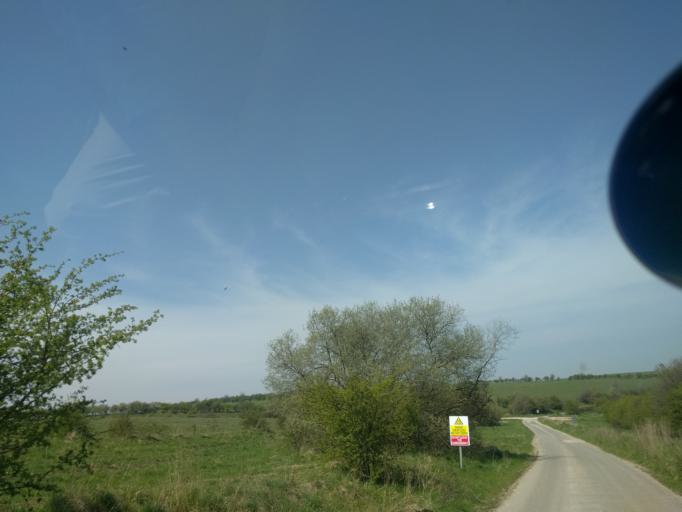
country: GB
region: England
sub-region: Wiltshire
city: Edington
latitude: 51.2487
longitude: -2.1024
